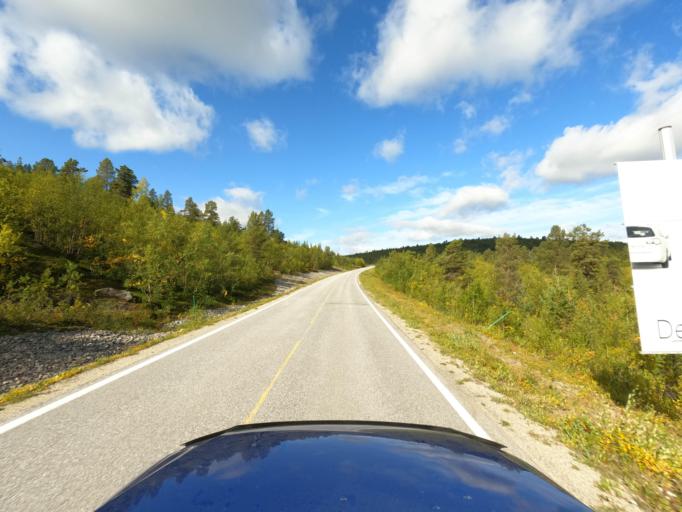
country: NO
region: Finnmark Fylke
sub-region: Karasjok
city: Karasjohka
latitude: 69.4853
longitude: 25.5080
